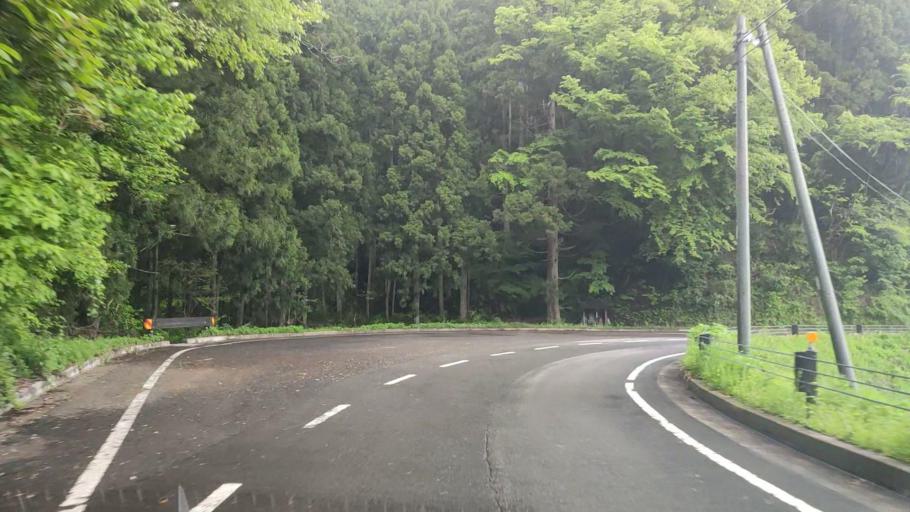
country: JP
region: Niigata
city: Gosen
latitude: 37.7154
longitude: 139.1239
